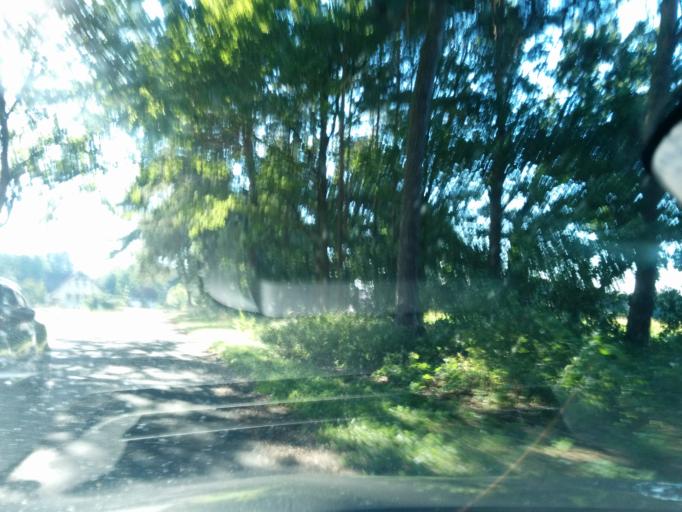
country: DE
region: Mecklenburg-Vorpommern
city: Eggesin
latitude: 53.6748
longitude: 14.0369
